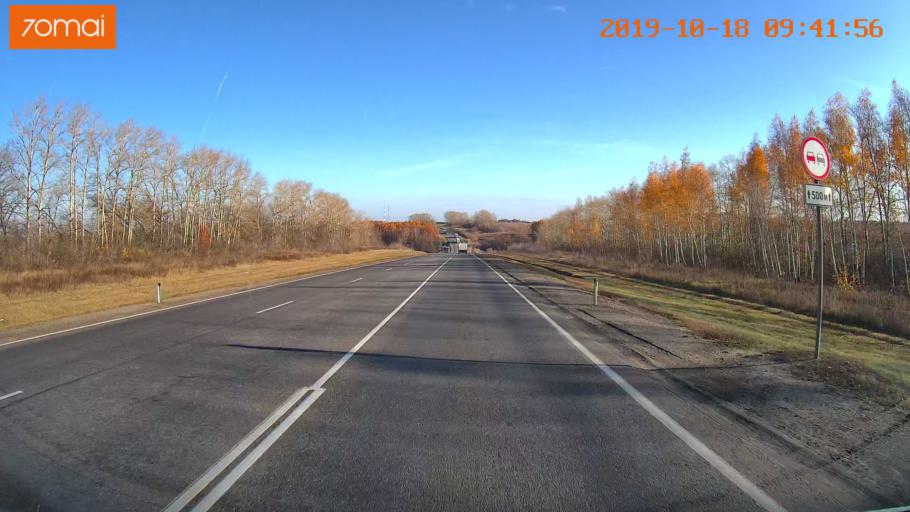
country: RU
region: Tula
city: Kazachka
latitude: 53.2808
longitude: 38.1692
